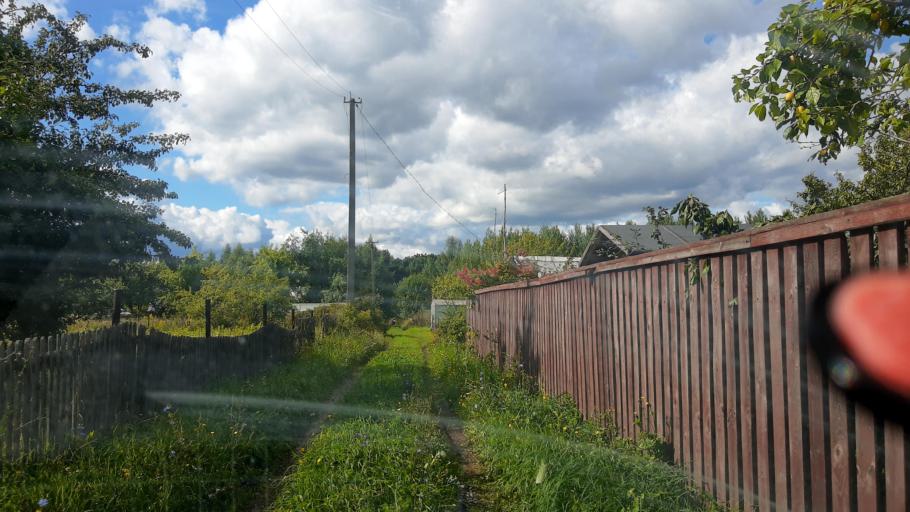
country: RU
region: Bashkortostan
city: Iglino
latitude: 54.7687
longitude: 56.4593
